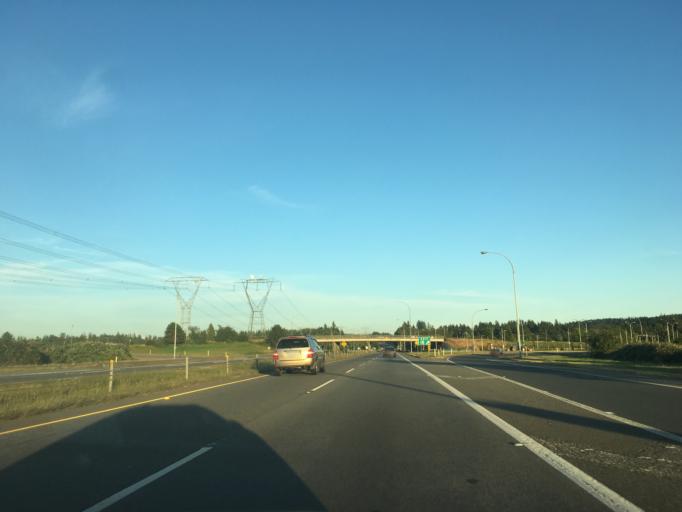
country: CA
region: British Columbia
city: Surrey
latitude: 49.0762
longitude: -122.8256
